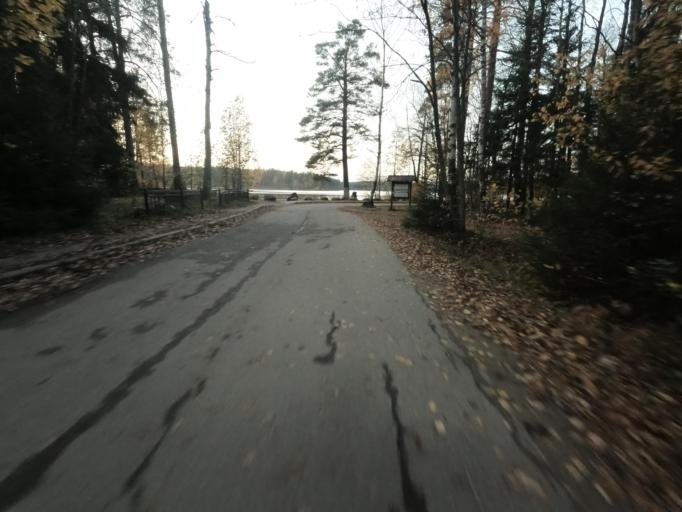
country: RU
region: St.-Petersburg
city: Komarovo
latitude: 60.2079
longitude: 29.7886
